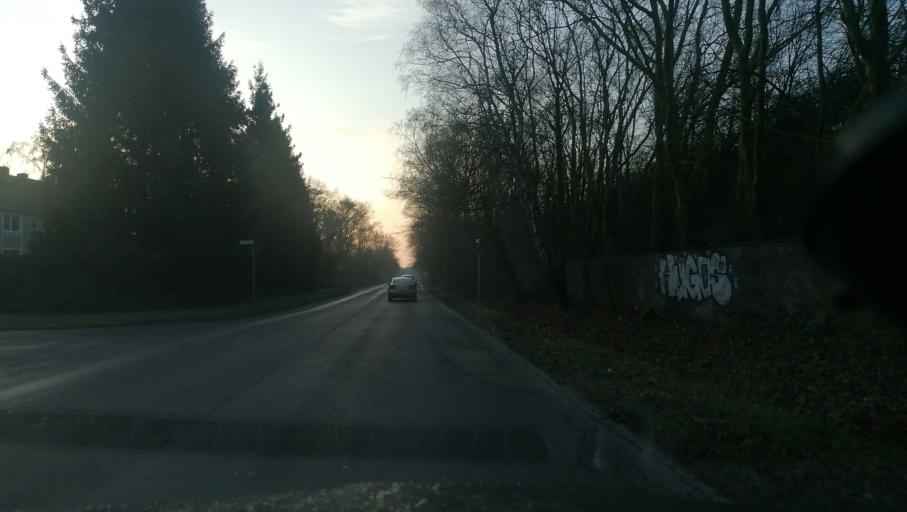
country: DE
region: North Rhine-Westphalia
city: Herten
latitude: 51.5686
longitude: 7.1345
